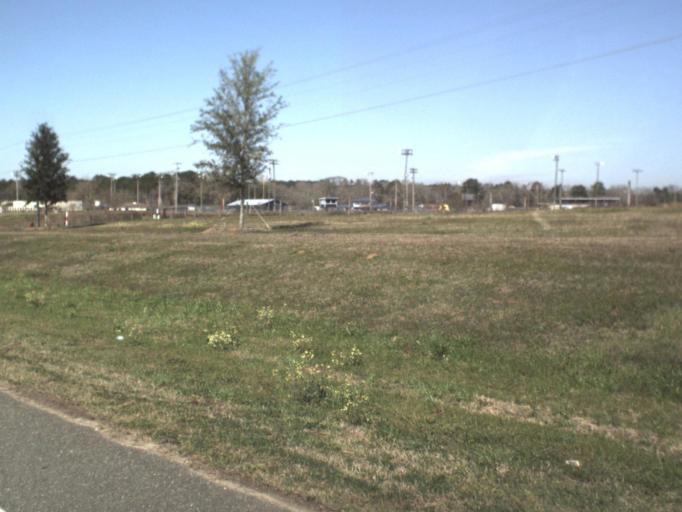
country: US
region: Florida
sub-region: Jackson County
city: Sneads
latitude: 30.7085
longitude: -84.9059
